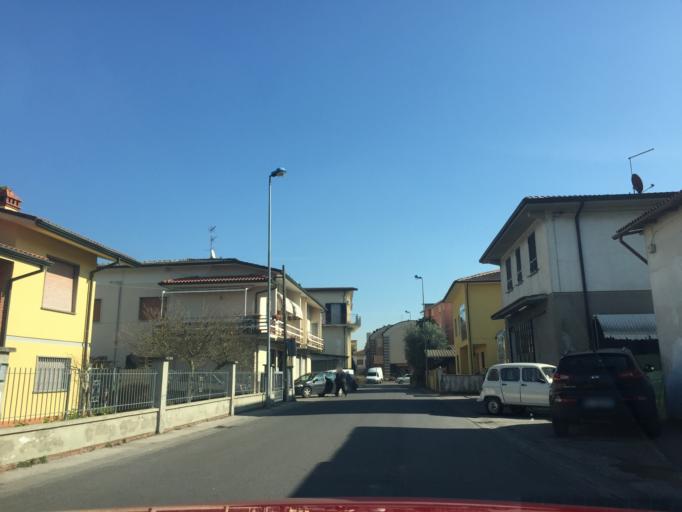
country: IT
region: Tuscany
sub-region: Provincia di Pistoia
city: Ponte Buggianese
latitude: 43.8437
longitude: 10.7462
